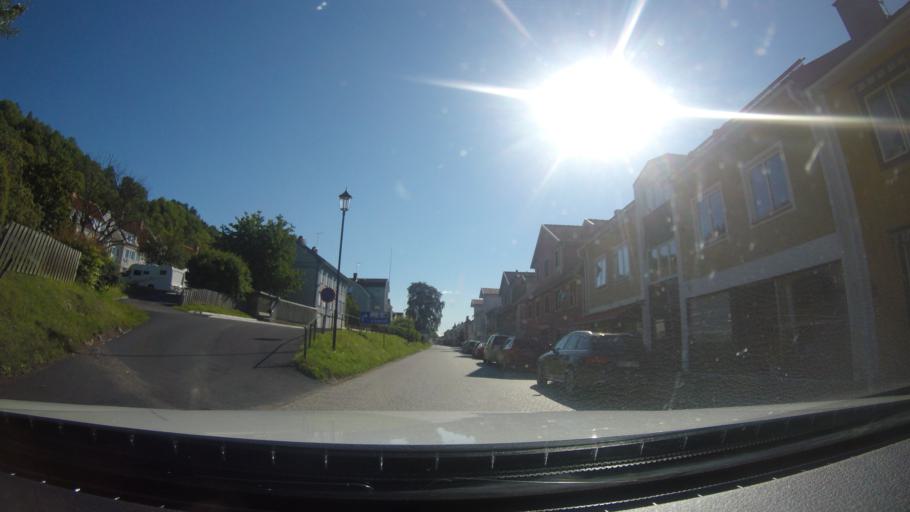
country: SE
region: Joenkoeping
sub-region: Jonkopings Kommun
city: Graenna
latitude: 58.0258
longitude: 14.4710
